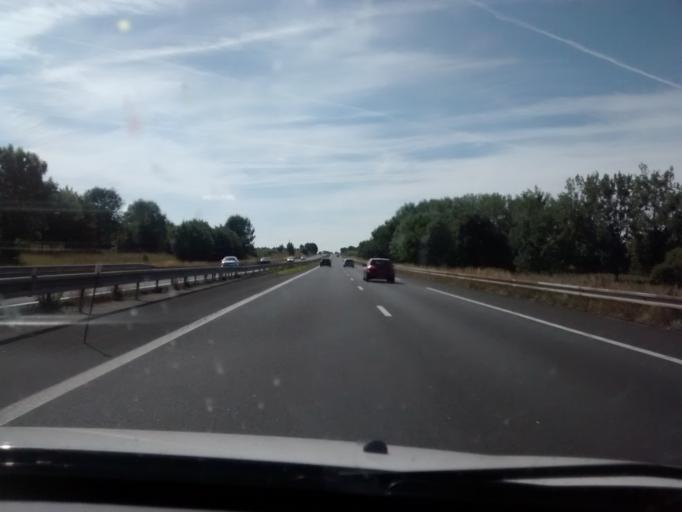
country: FR
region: Pays de la Loire
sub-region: Departement de la Mayenne
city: Soulge-sur-Ouette
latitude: 48.0634
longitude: -0.5309
